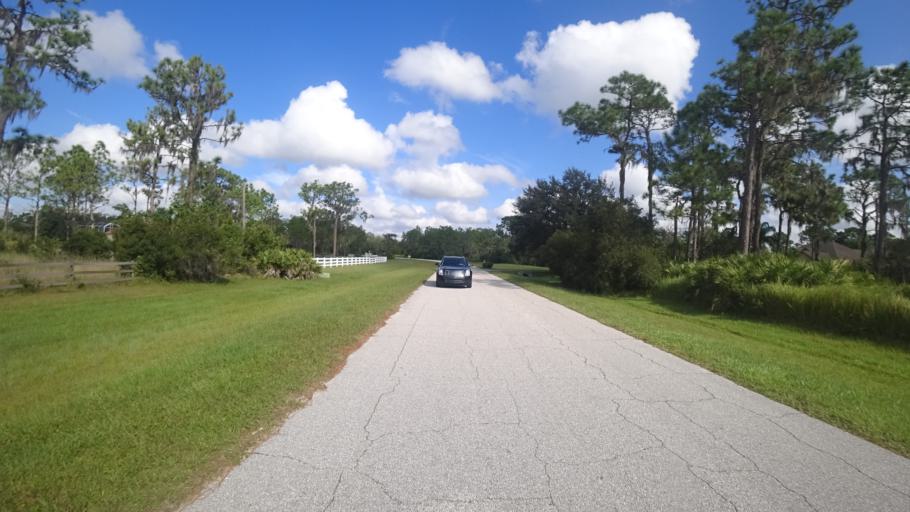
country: US
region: Florida
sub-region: Sarasota County
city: The Meadows
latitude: 27.4034
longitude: -82.3244
